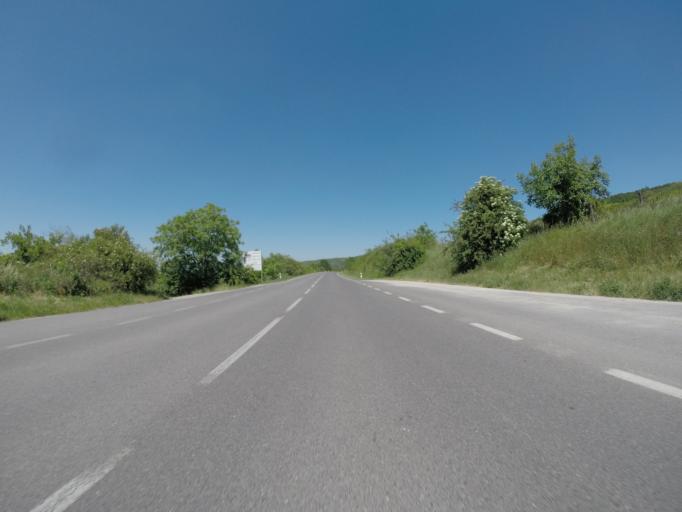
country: SK
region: Trnavsky
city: Hlohovec
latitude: 48.4570
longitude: 17.8136
